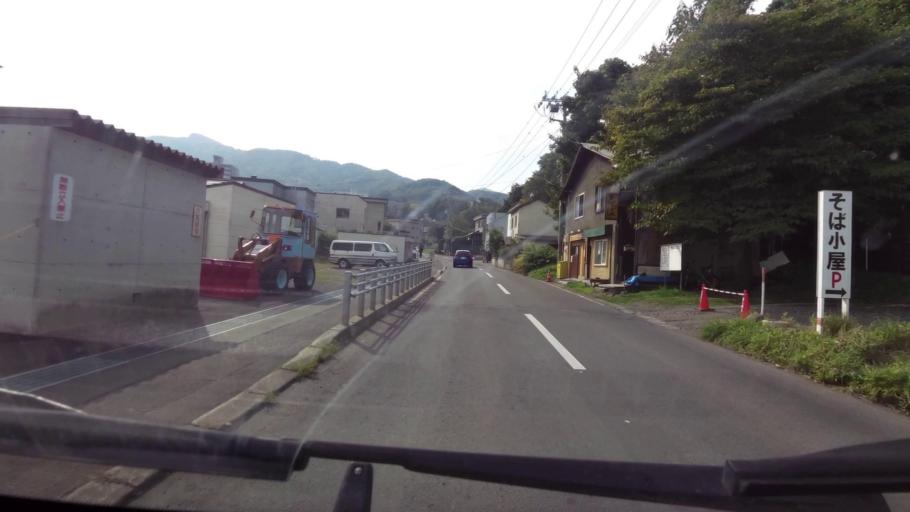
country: JP
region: Hokkaido
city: Otaru
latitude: 43.1438
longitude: 141.1579
